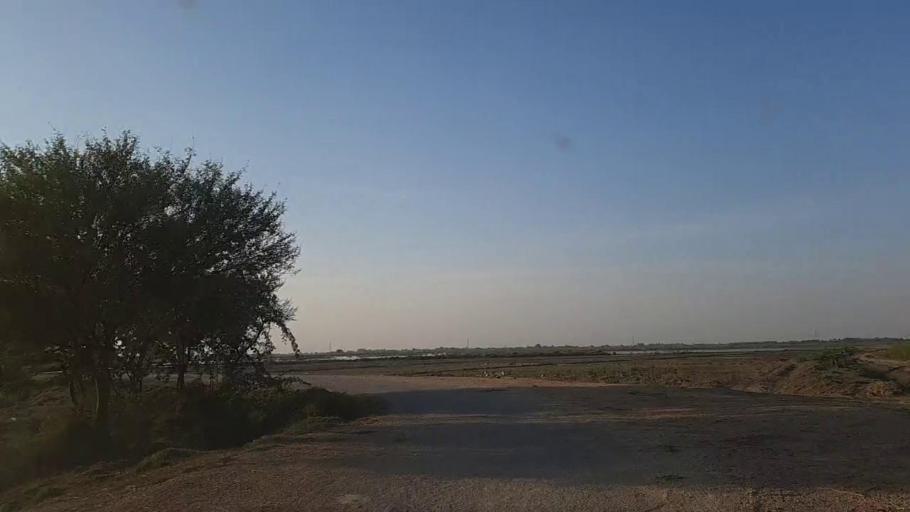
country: PK
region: Sindh
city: Mirpur Batoro
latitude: 24.6847
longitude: 68.2089
